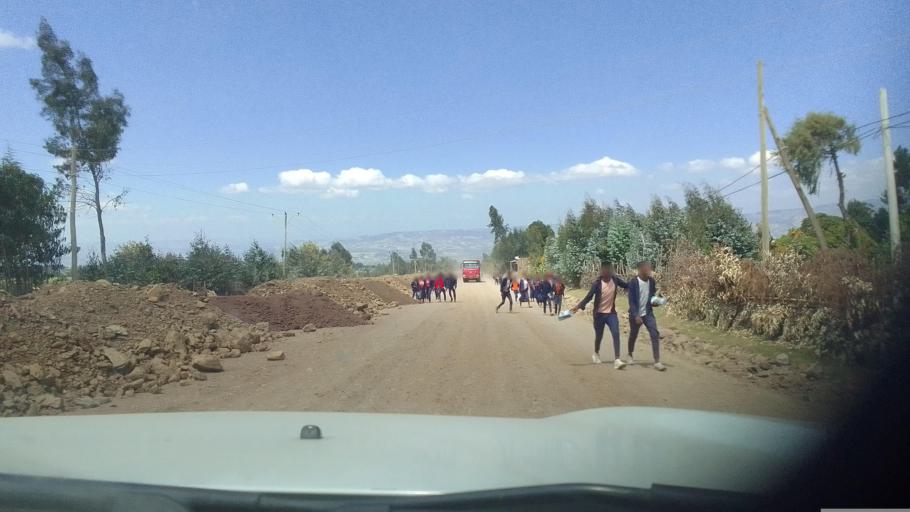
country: ET
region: Oromiya
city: Hagere Hiywet
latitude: 8.8553
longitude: 37.8927
